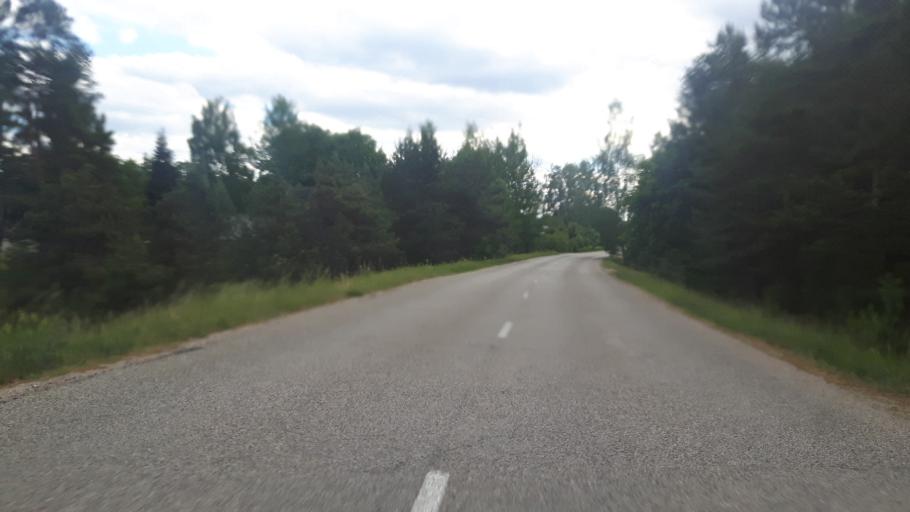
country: LV
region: Engure
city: Smarde
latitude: 57.0375
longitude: 23.3746
